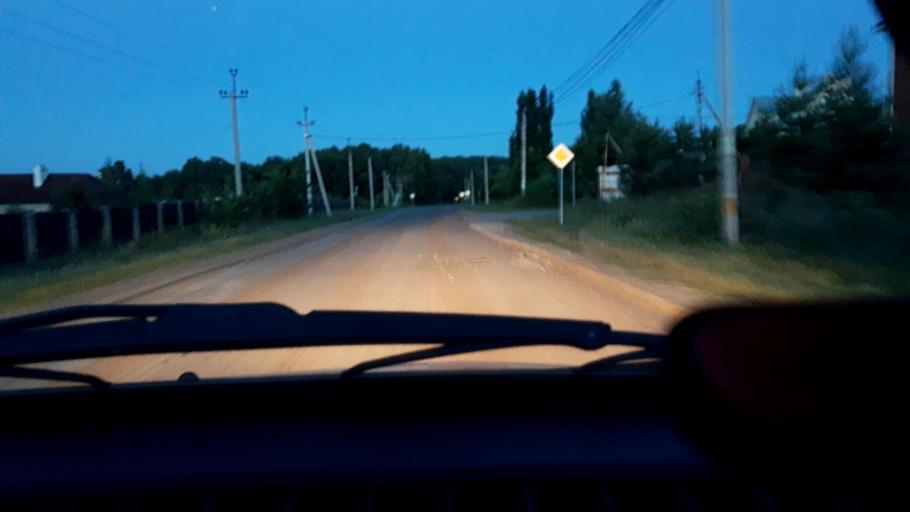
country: RU
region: Bashkortostan
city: Avdon
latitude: 54.6416
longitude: 55.7024
